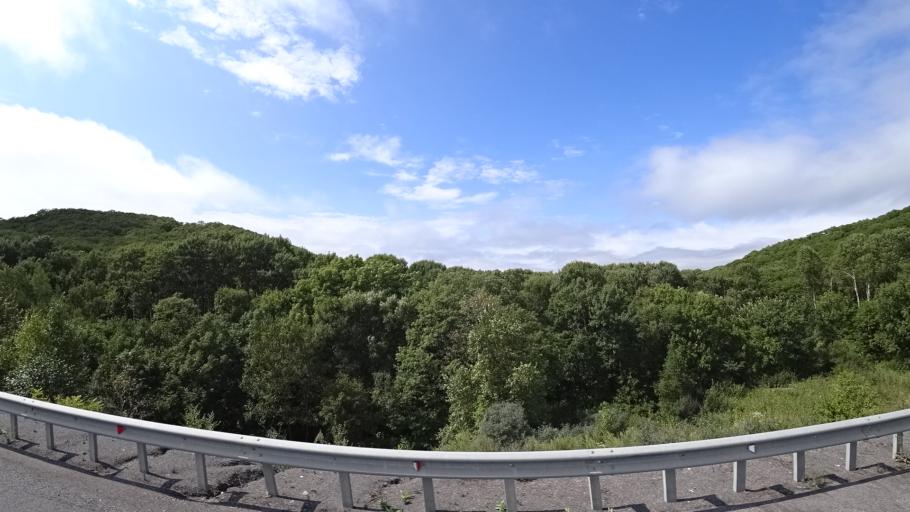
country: RU
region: Primorskiy
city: Lyalichi
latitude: 44.1260
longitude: 132.4242
